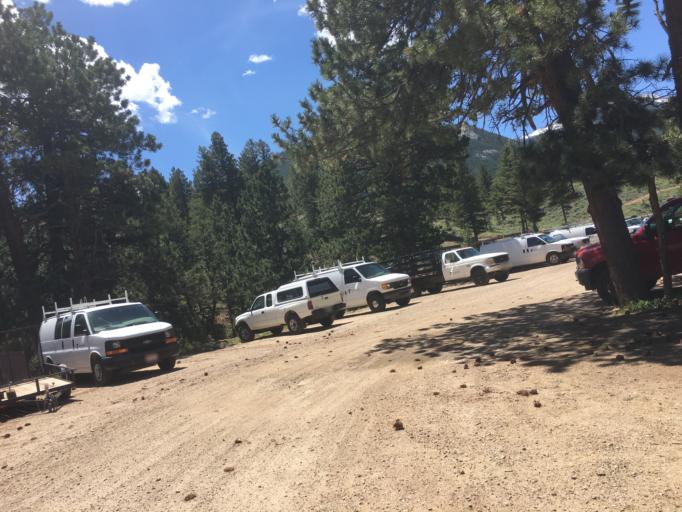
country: US
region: Colorado
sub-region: Larimer County
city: Estes Park
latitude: 40.3381
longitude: -105.5701
